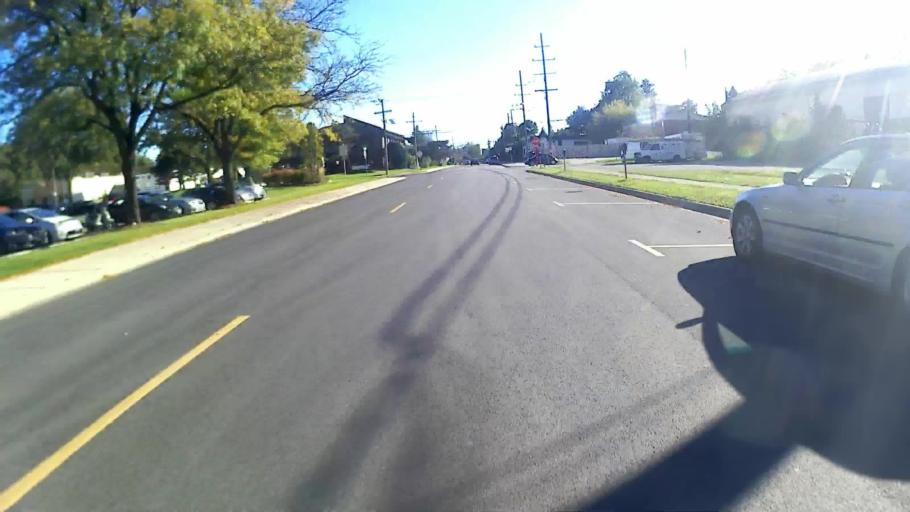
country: US
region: Illinois
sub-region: DuPage County
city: Wheaton
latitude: 41.8629
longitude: -88.1162
